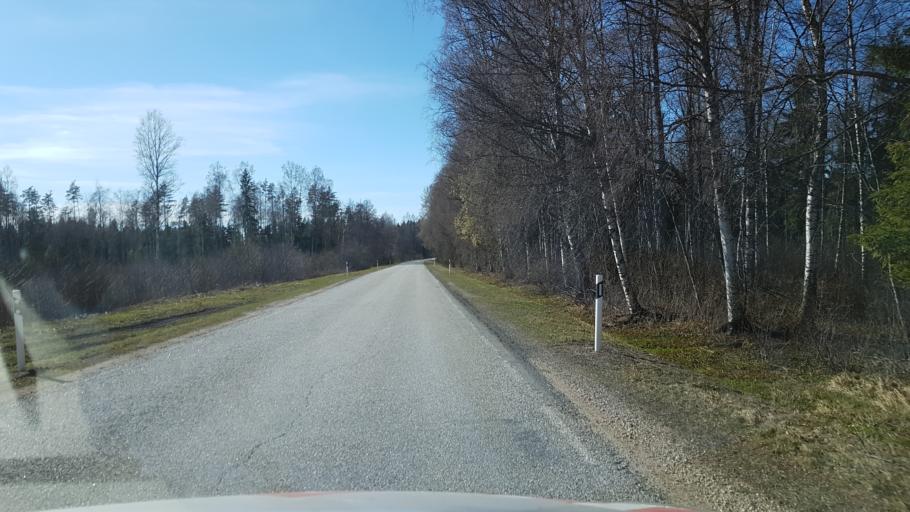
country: EE
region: Ida-Virumaa
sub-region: Aseri vald
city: Aseri
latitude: 59.2299
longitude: 26.7142
